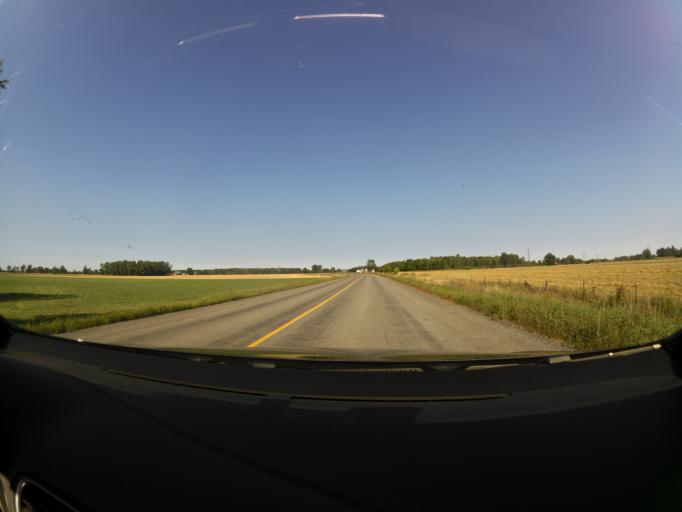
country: CA
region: Ontario
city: Arnprior
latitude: 45.3769
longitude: -76.3302
